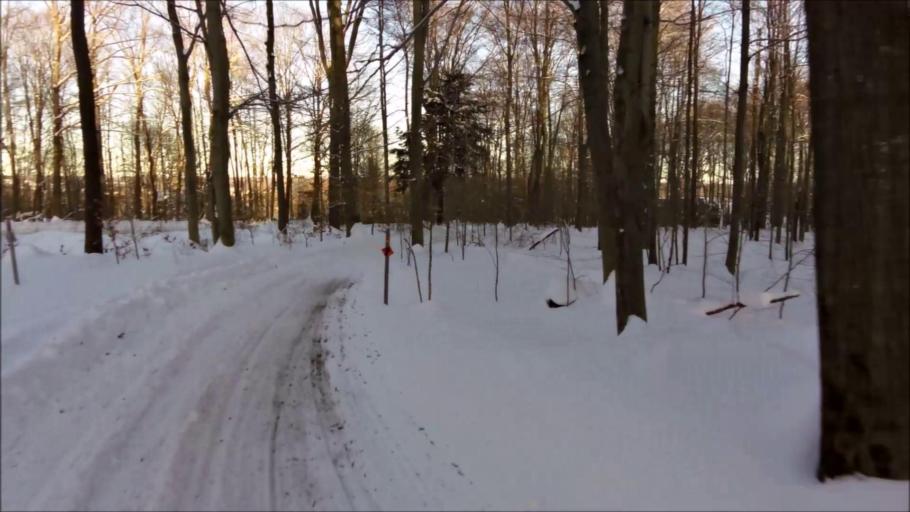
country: US
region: New York
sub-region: Chautauqua County
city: Celoron
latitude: 42.2279
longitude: -79.3063
